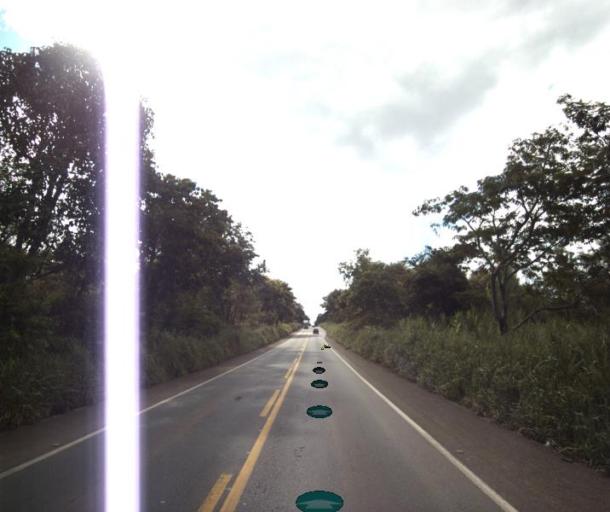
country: BR
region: Goias
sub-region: Jaragua
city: Jaragua
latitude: -15.6720
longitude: -49.3481
